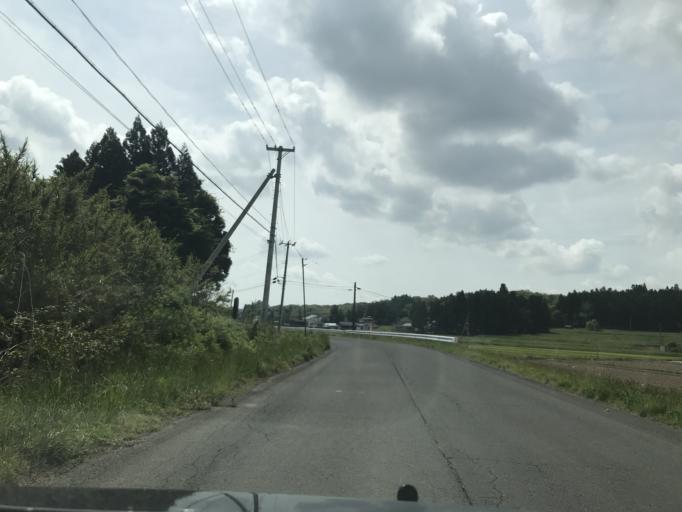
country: JP
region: Iwate
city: Ichinoseki
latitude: 38.8534
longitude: 141.0072
